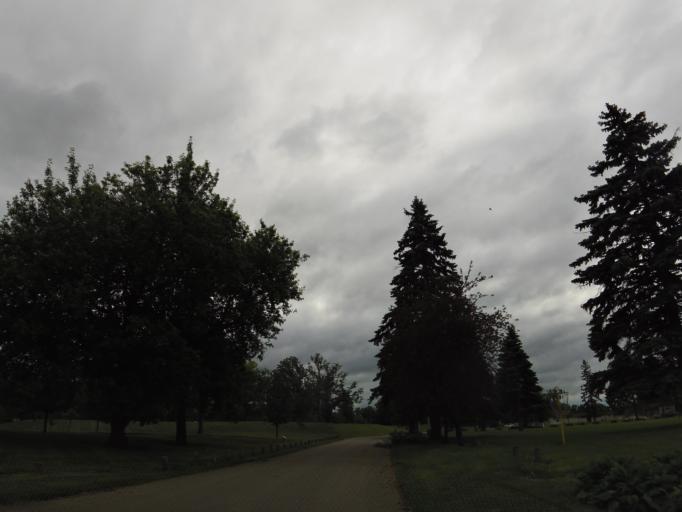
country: US
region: North Dakota
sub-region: Walsh County
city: Grafton
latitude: 48.4228
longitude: -97.4166
